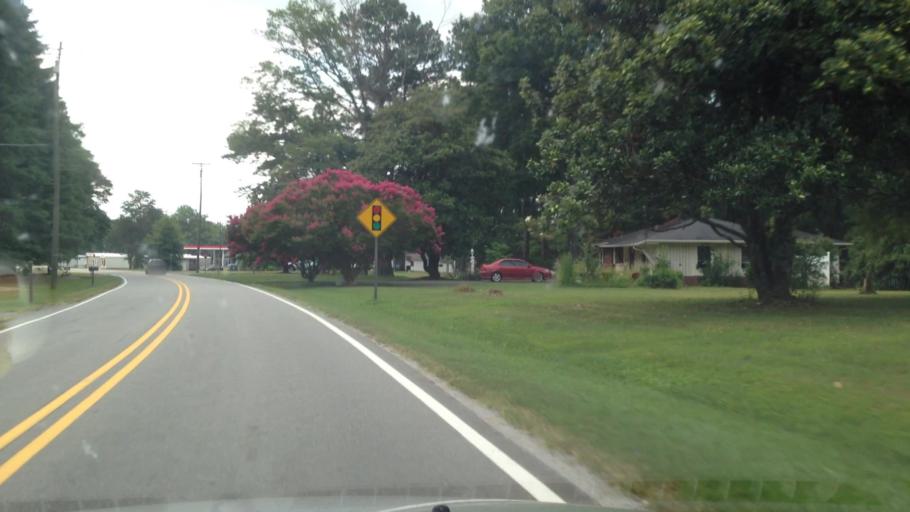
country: US
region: North Carolina
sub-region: Rockingham County
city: Madison
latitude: 36.3837
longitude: -80.0021
